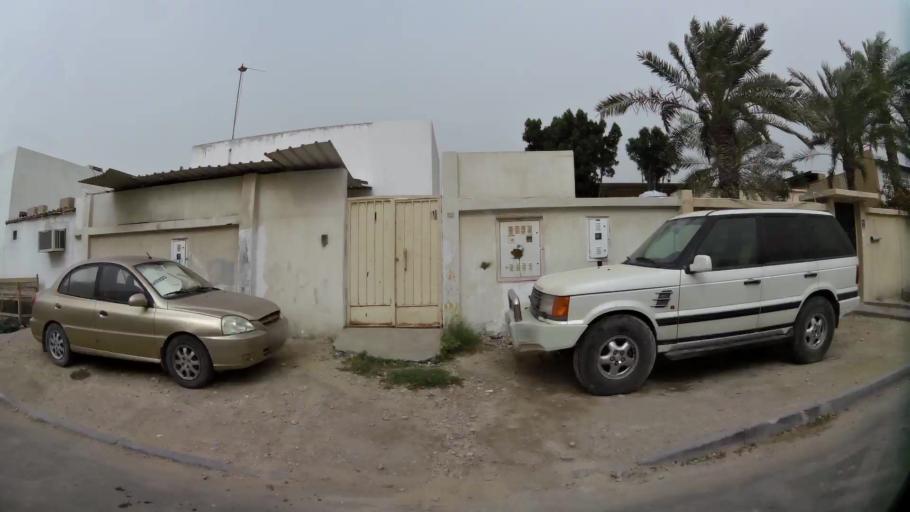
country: QA
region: Baladiyat ad Dawhah
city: Doha
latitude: 25.2497
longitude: 51.5138
